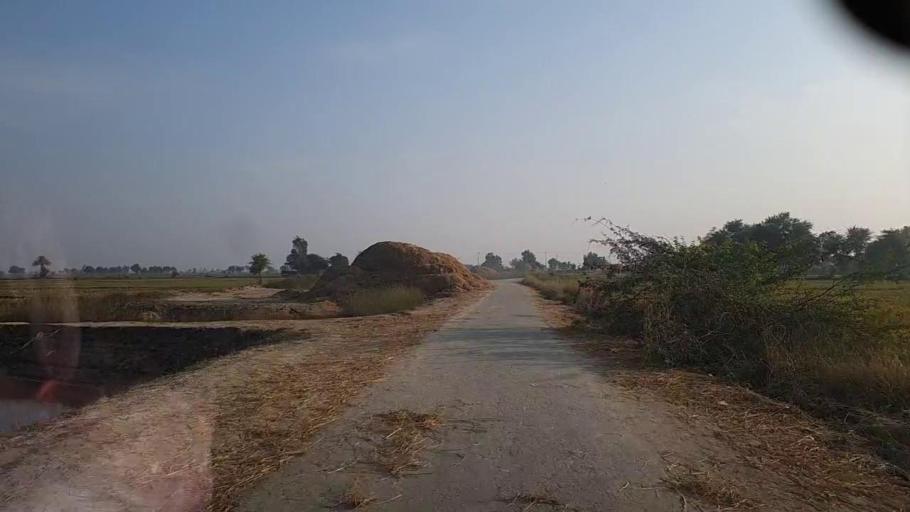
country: PK
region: Sindh
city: Jacobabad
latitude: 28.2339
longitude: 68.4861
